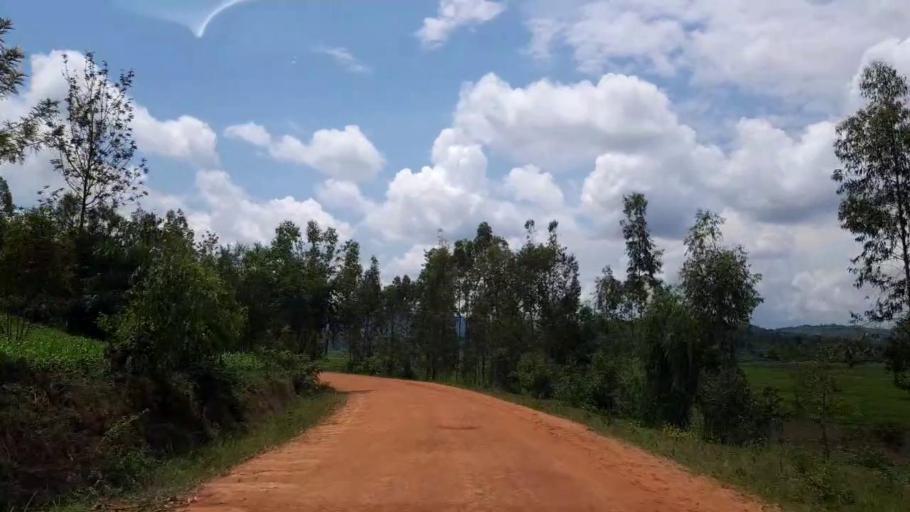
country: RW
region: Northern Province
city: Byumba
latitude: -1.5677
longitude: 30.2978
